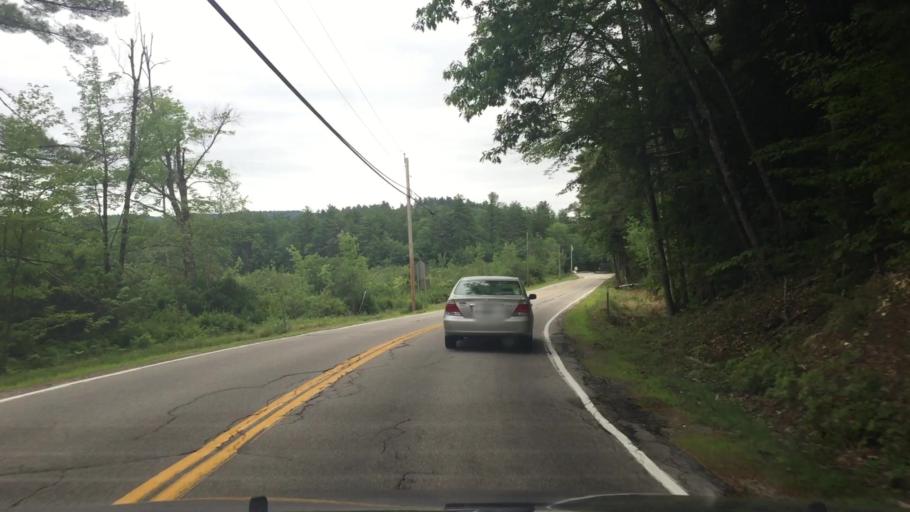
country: US
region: New Hampshire
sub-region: Carroll County
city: Conway
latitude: 43.9203
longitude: -71.0741
